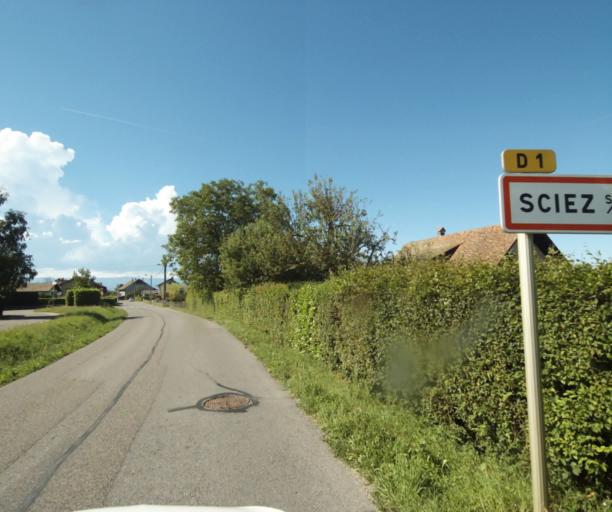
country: FR
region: Rhone-Alpes
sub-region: Departement de la Haute-Savoie
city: Sciez
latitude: 46.3257
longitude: 6.3811
